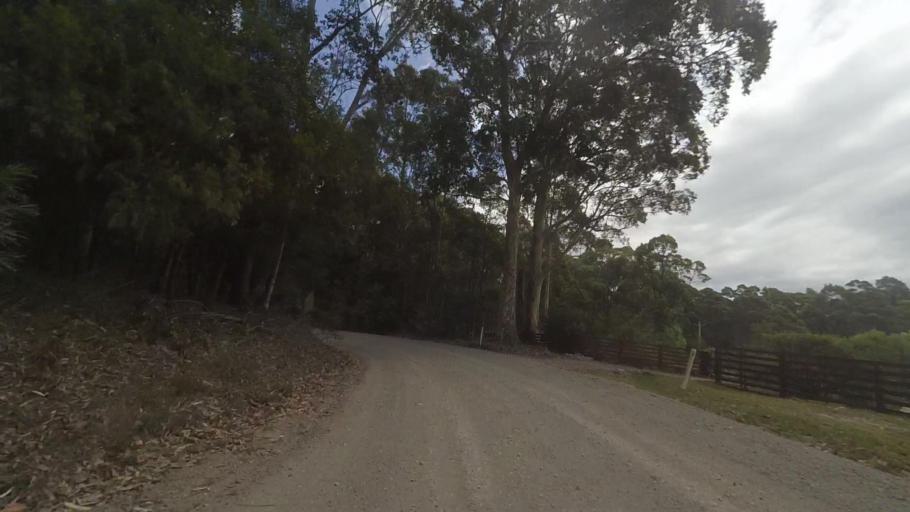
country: AU
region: New South Wales
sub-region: Shoalhaven Shire
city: Milton
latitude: -35.4371
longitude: 150.3286
